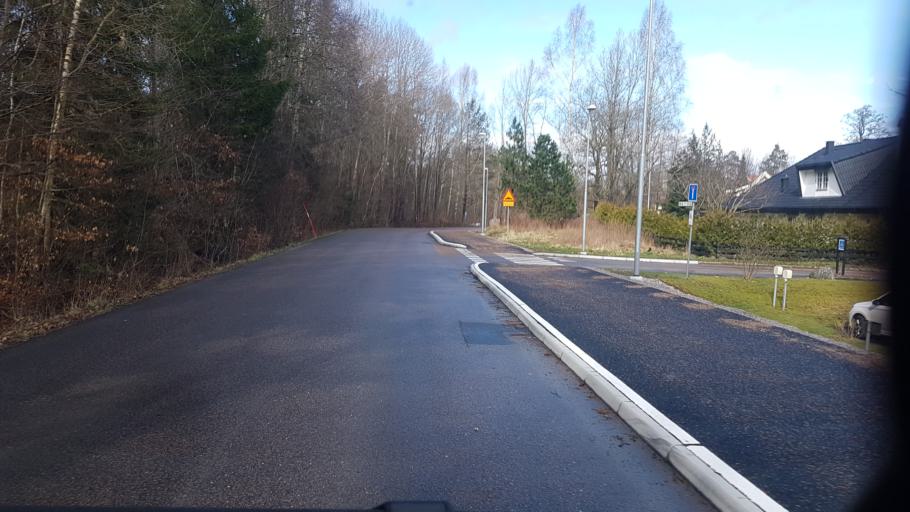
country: SE
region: Vaestra Goetaland
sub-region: Lerums Kommun
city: Stenkullen
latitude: 57.8088
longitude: 12.3722
